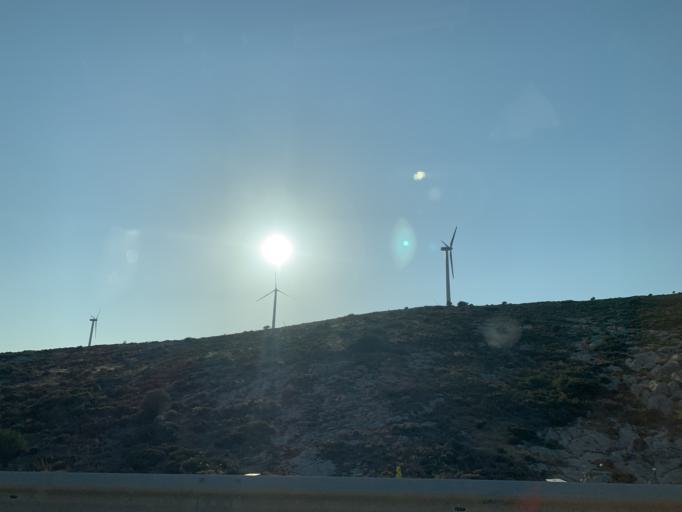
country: TR
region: Izmir
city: Alacati
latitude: 38.2818
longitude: 26.4012
